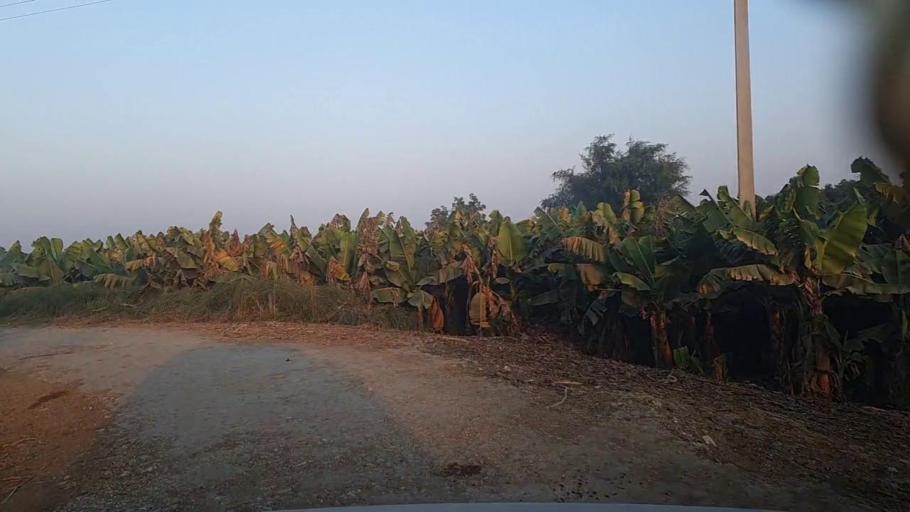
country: PK
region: Sindh
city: Karaundi
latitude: 26.8430
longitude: 68.3610
